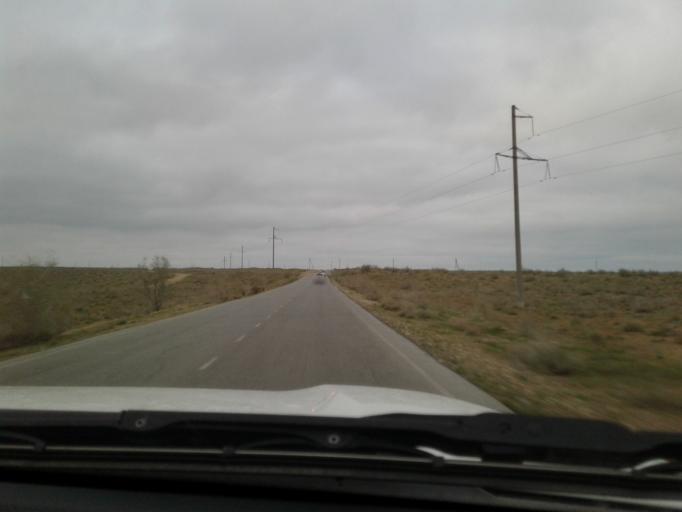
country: TM
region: Lebap
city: Farap
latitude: 39.0920
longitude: 63.7212
